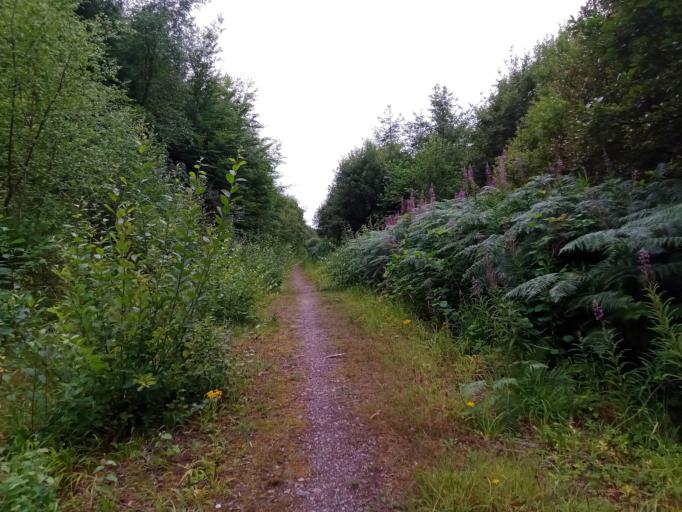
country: IE
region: Leinster
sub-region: Kilkenny
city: Ballyragget
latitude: 52.8196
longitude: -7.4154
